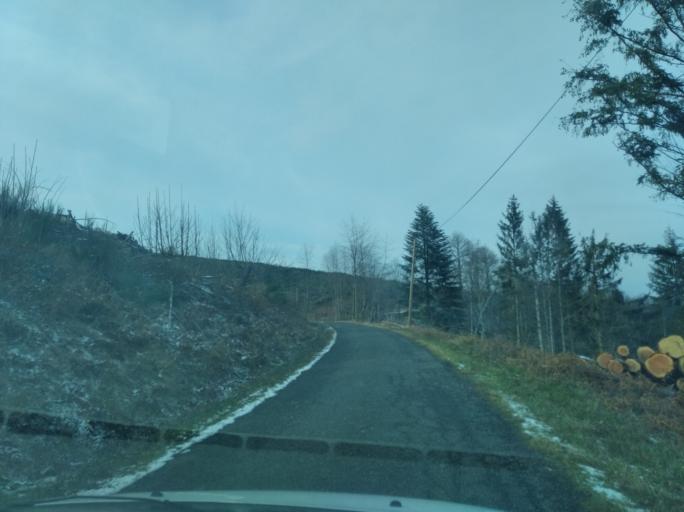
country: FR
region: Rhone-Alpes
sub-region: Departement de la Loire
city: La Pacaudiere
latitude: 46.1383
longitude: 3.7773
